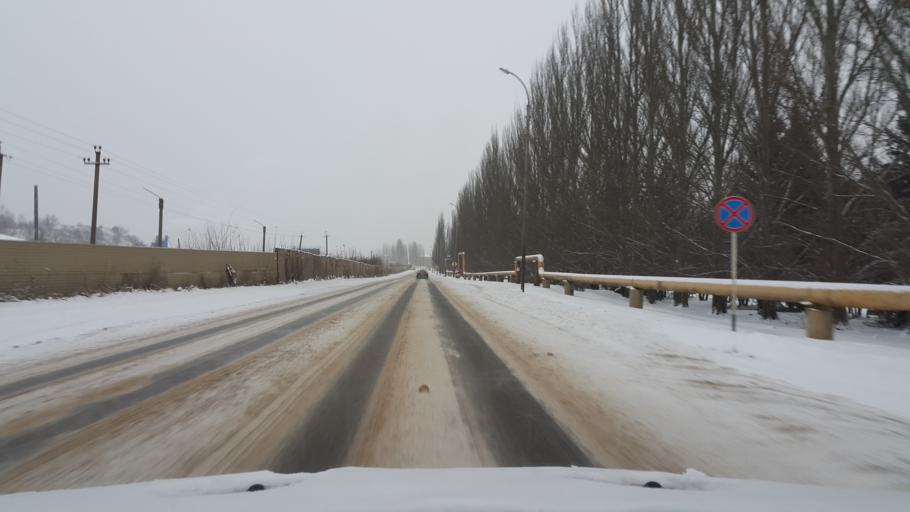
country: RU
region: Tambov
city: Pokrovo-Prigorodnoye
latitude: 52.6604
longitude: 41.4124
